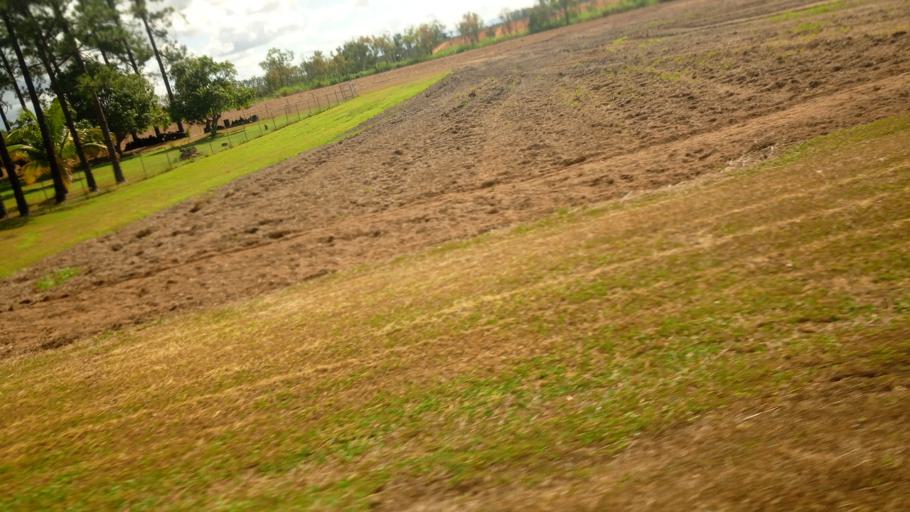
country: AU
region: Queensland
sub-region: Tablelands
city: Mareeba
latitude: -17.0154
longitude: 145.3612
